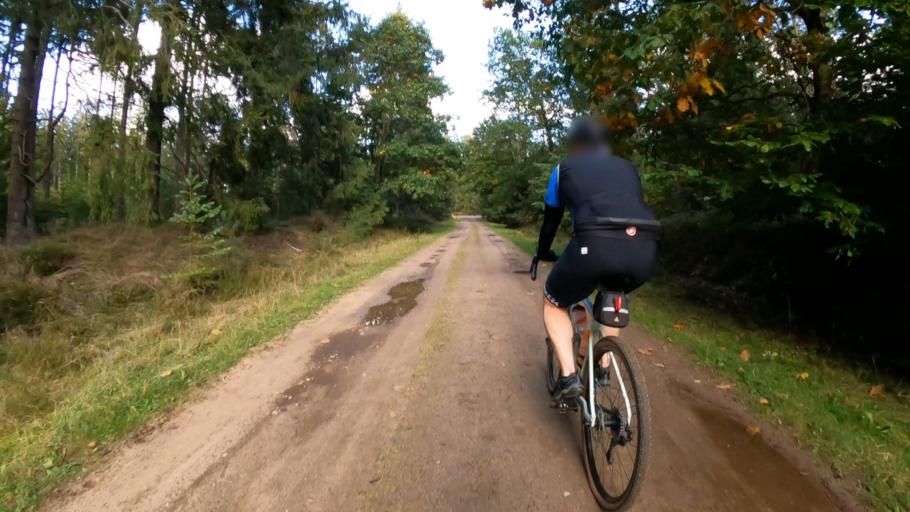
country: DE
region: Schleswig-Holstein
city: Hartenholm
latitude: 53.9329
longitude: 10.0809
